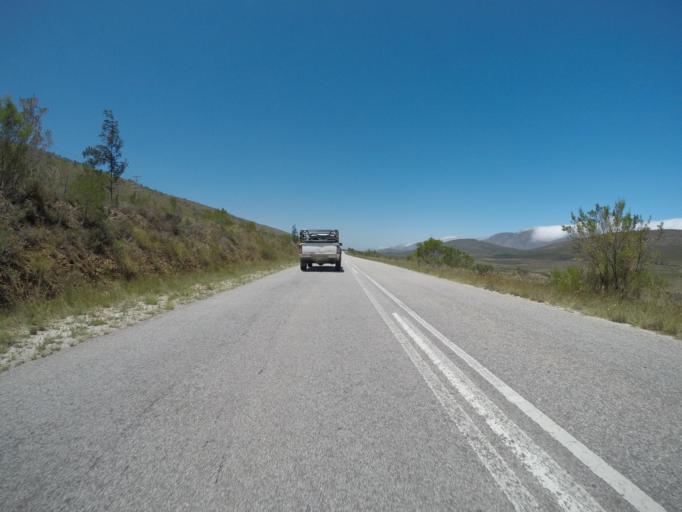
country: ZA
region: Eastern Cape
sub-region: Cacadu District Municipality
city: Kareedouw
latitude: -33.8408
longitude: 23.9334
